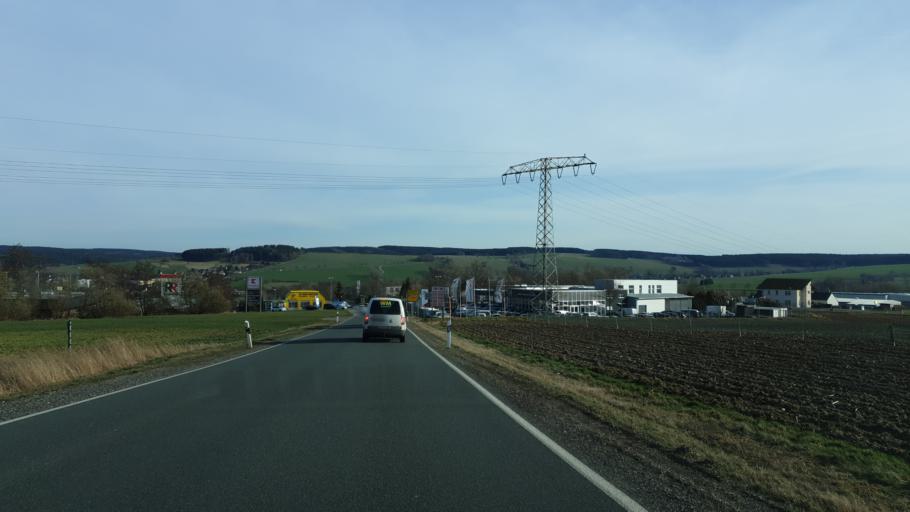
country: DE
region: Saxony
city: Zwonitz
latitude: 50.6368
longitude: 12.7920
